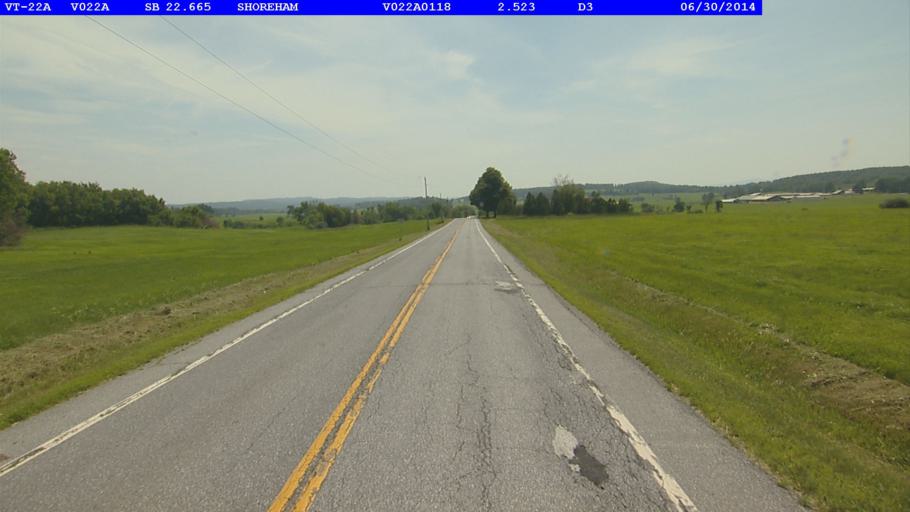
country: US
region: New York
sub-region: Essex County
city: Ticonderoga
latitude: 43.8859
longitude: -73.3094
